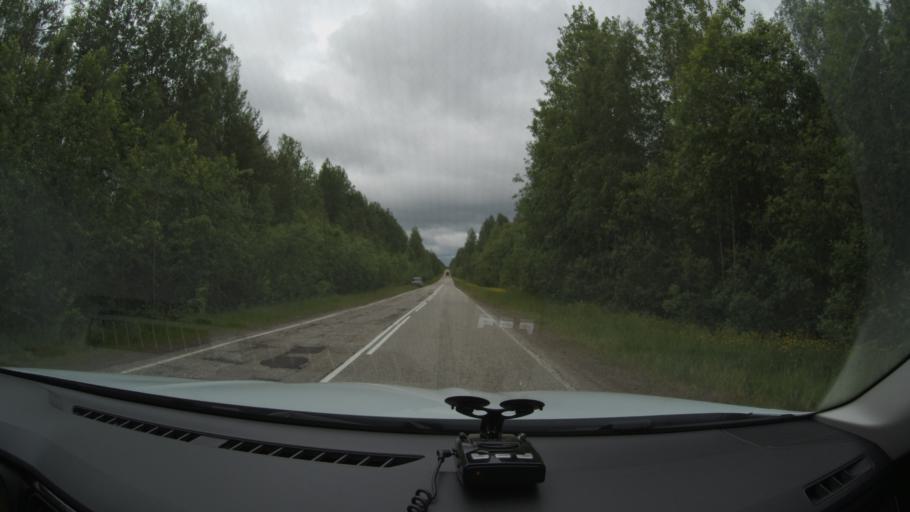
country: RU
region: Komi Republic
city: Nizhniy Odes
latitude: 63.6062
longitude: 54.5463
